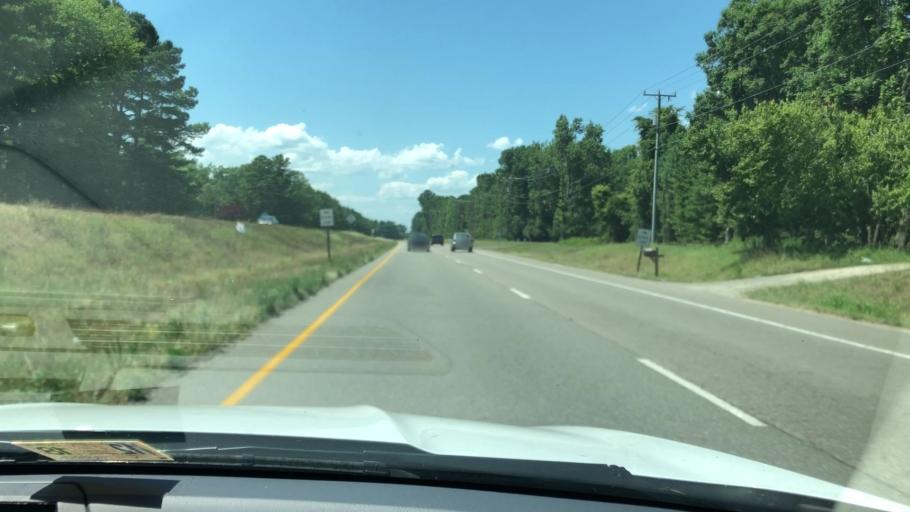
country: US
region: Virginia
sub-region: Middlesex County
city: Saluda
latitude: 37.5939
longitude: -76.5007
